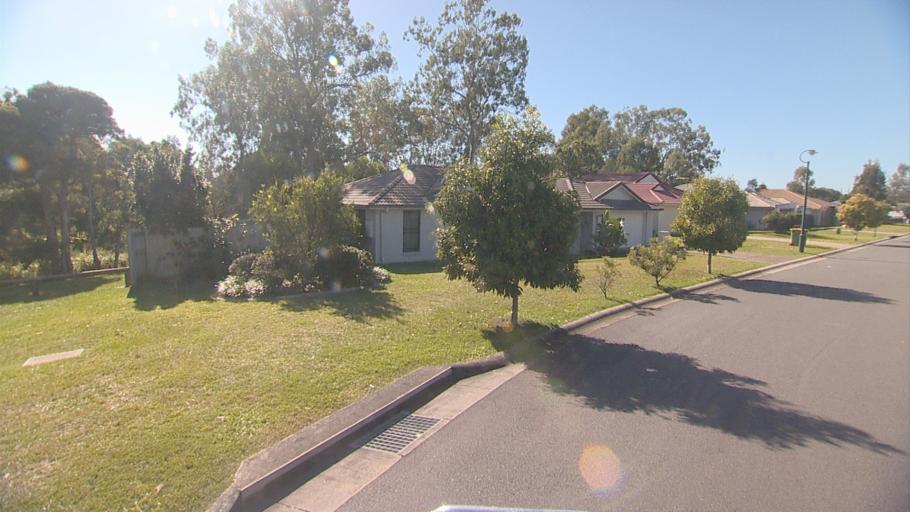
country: AU
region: Queensland
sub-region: Logan
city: Logan City
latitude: -27.6293
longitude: 153.1217
